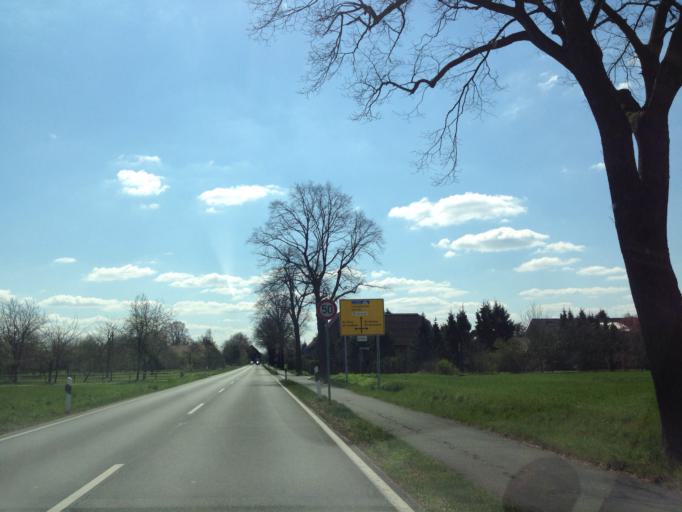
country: DE
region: North Rhine-Westphalia
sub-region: Regierungsbezirk Munster
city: Muenster
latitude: 51.8983
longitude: 7.5814
